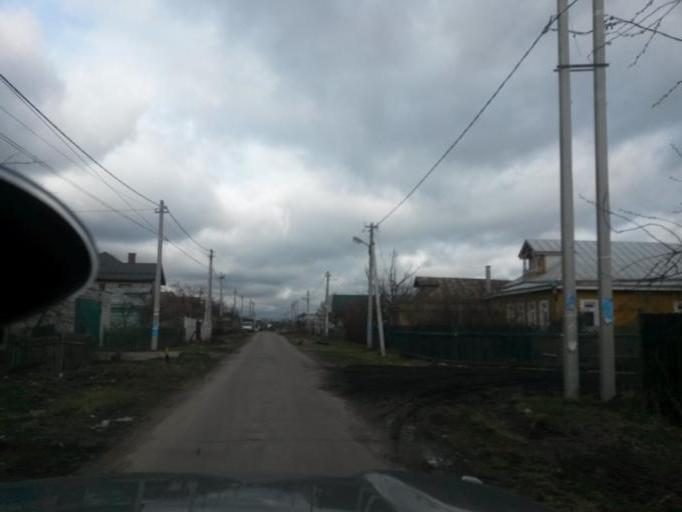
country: RU
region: Moskovskaya
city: Alekseyevka
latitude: 55.6032
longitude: 37.8241
